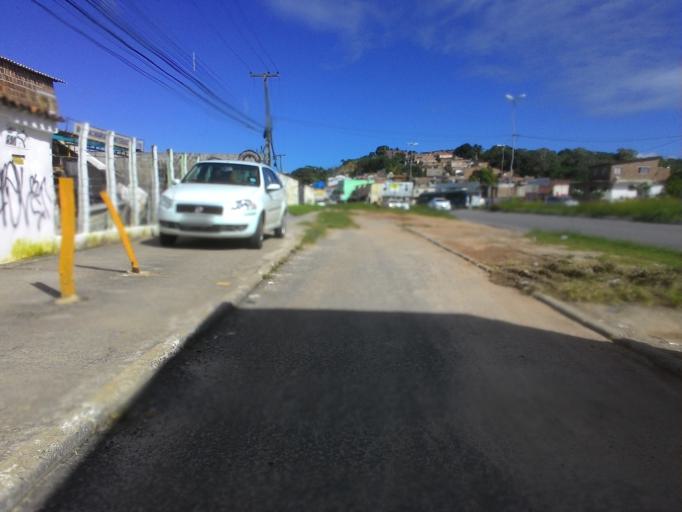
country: BR
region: Pernambuco
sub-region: Olinda
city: Olinda
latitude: -7.9754
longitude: -34.8636
